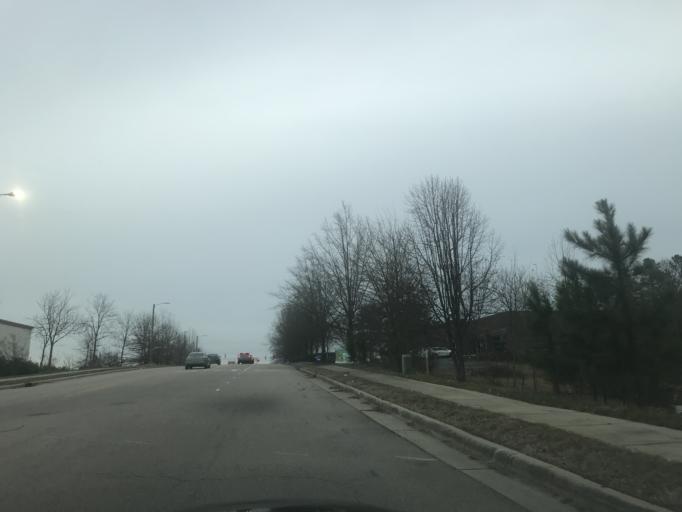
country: US
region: North Carolina
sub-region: Wake County
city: Raleigh
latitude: 35.8712
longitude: -78.5846
